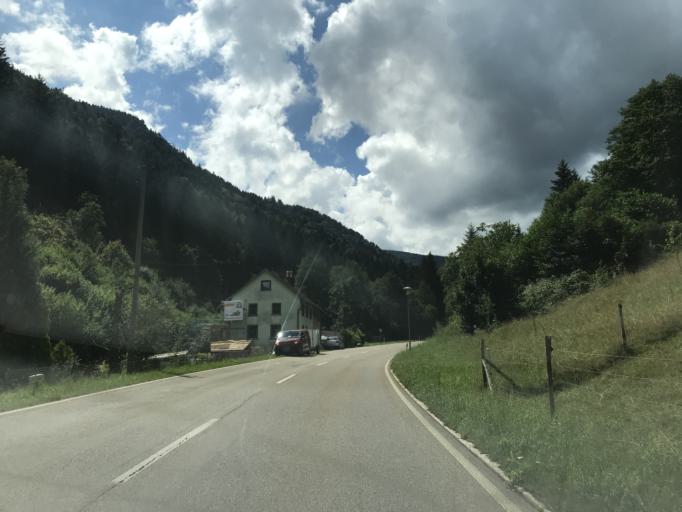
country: DE
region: Baden-Wuerttemberg
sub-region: Freiburg Region
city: Oberried
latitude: 47.9220
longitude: 7.9380
